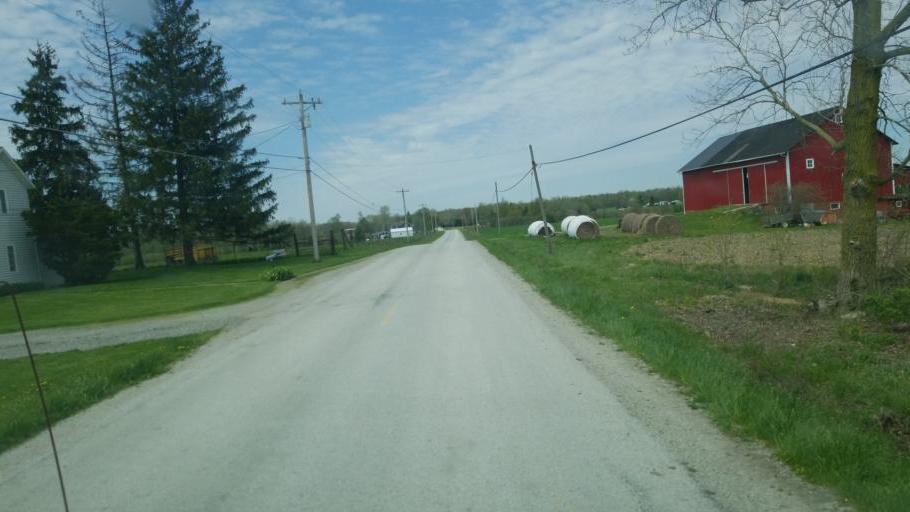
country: US
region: Ohio
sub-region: Hardin County
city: Ada
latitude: 40.7081
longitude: -83.7893
